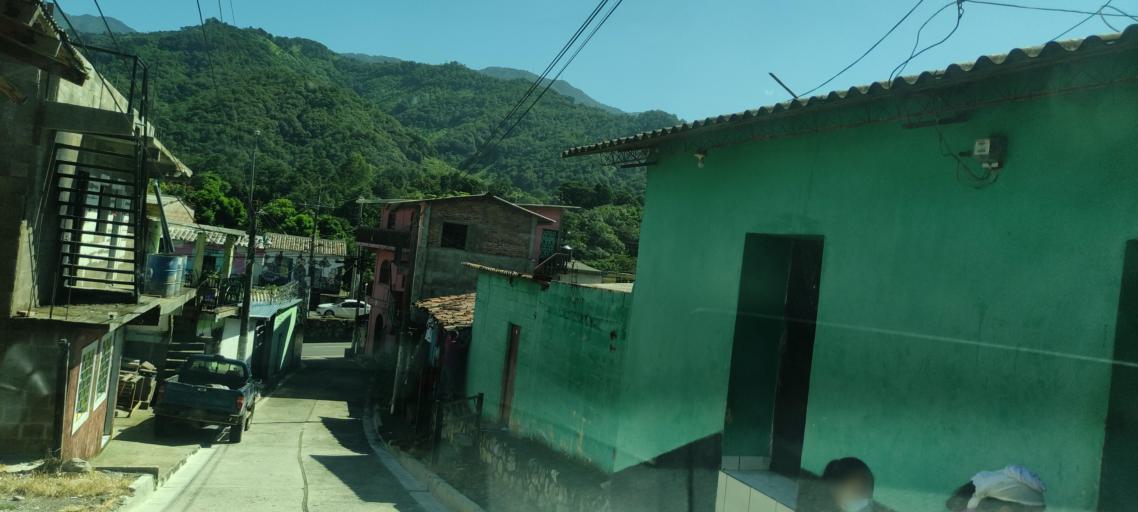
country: HN
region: Ocotepeque
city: Antigua Ocotepeque
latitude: 14.3152
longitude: -89.1691
